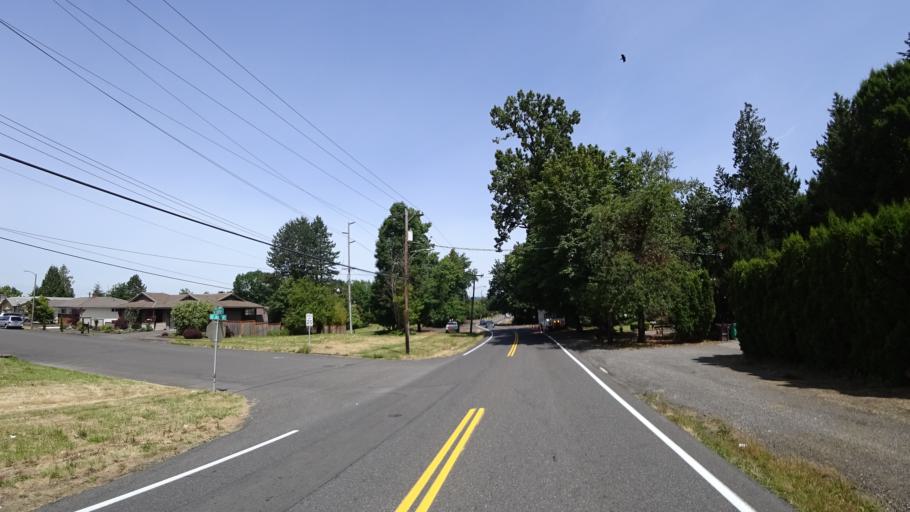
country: US
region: Oregon
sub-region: Multnomah County
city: Fairview
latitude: 45.5454
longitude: -122.4957
